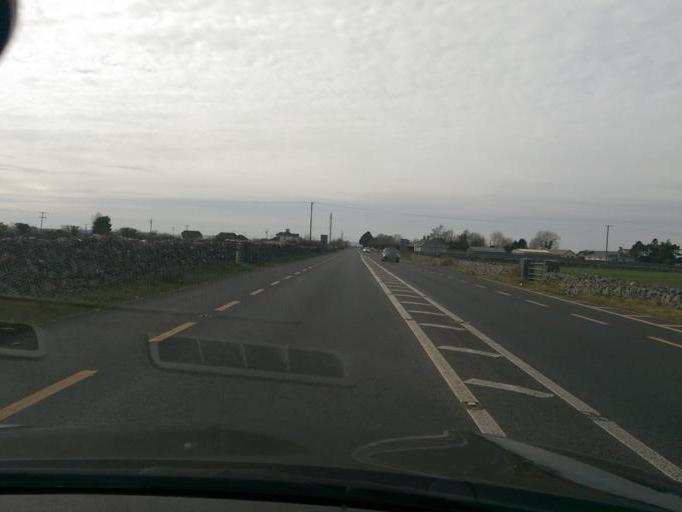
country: IE
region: Connaught
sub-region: County Galway
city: Claregalway
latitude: 53.3631
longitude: -8.9143
